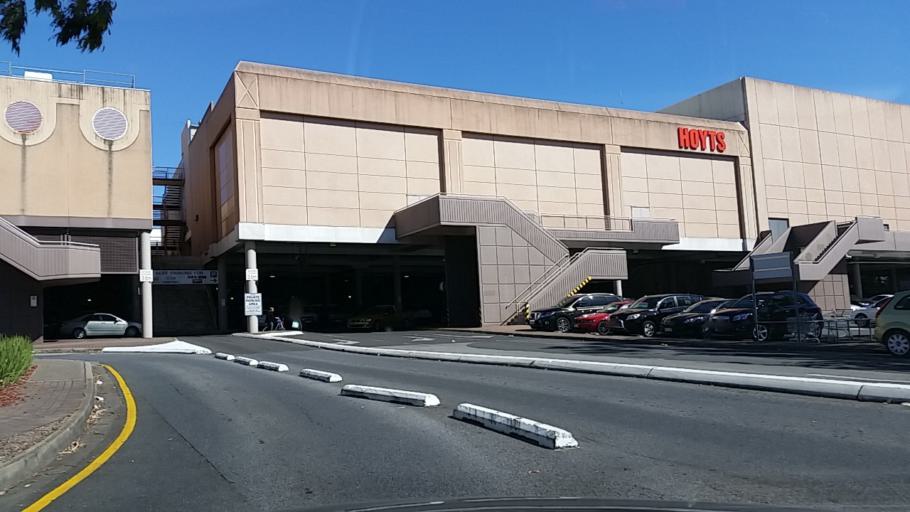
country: AU
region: South Australia
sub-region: Tea Tree Gully
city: Modbury
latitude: -34.8304
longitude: 138.6900
